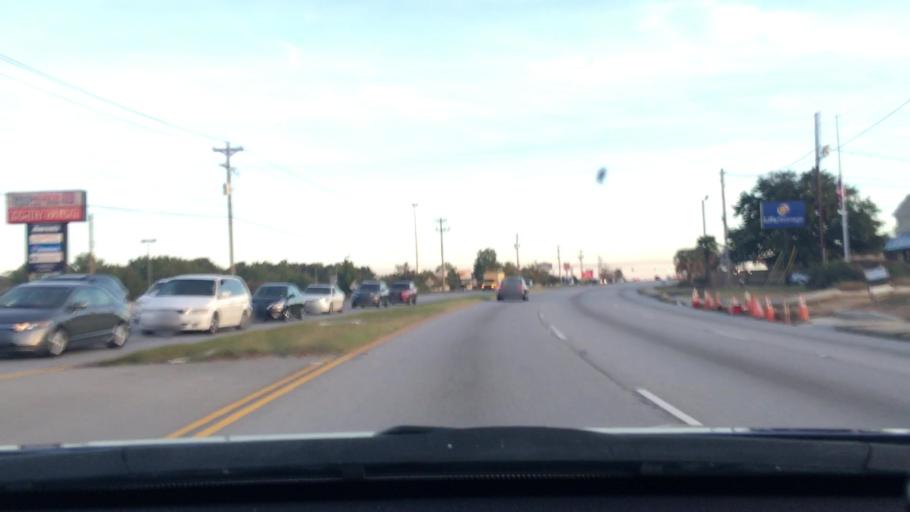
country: US
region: South Carolina
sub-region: Richland County
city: Forest Acres
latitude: 33.9687
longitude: -80.9459
